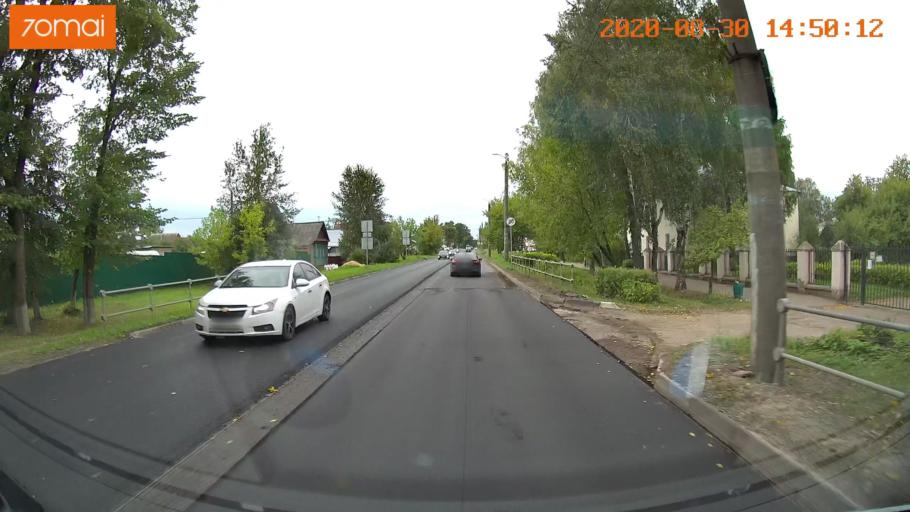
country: RU
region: Ivanovo
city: Kineshma
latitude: 57.4296
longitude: 42.0981
